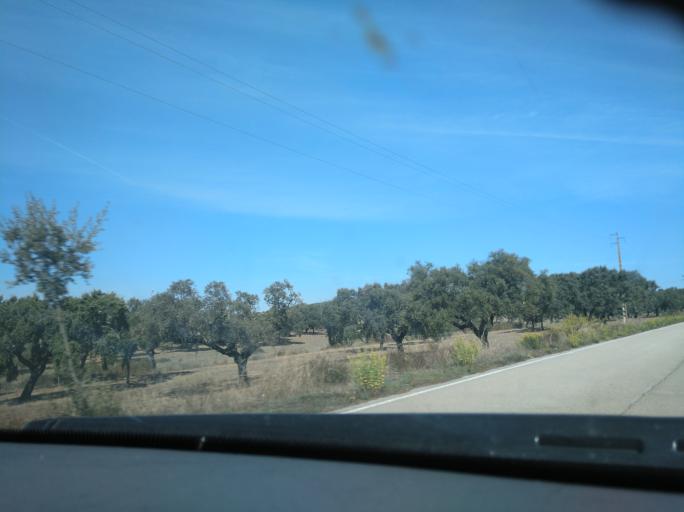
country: PT
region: Evora
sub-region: Arraiolos
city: Arraiolos
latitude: 38.6855
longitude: -8.0906
